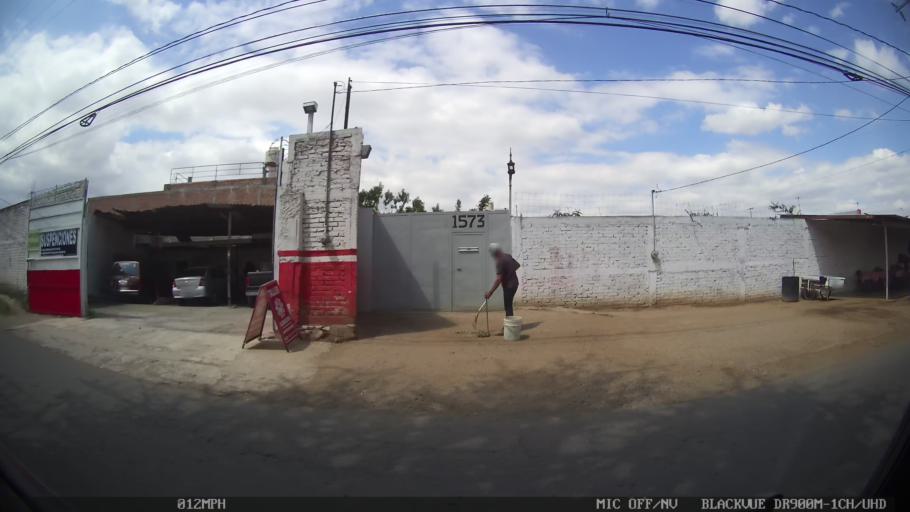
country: MX
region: Jalisco
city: Tonala
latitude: 20.6401
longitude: -103.2566
